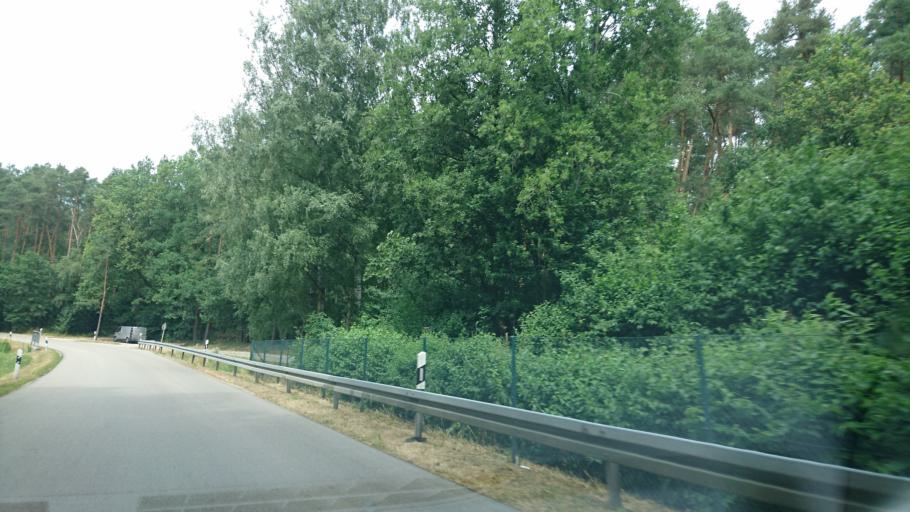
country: DE
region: Bavaria
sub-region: Regierungsbezirk Mittelfranken
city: Roth
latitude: 49.2098
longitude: 11.0847
